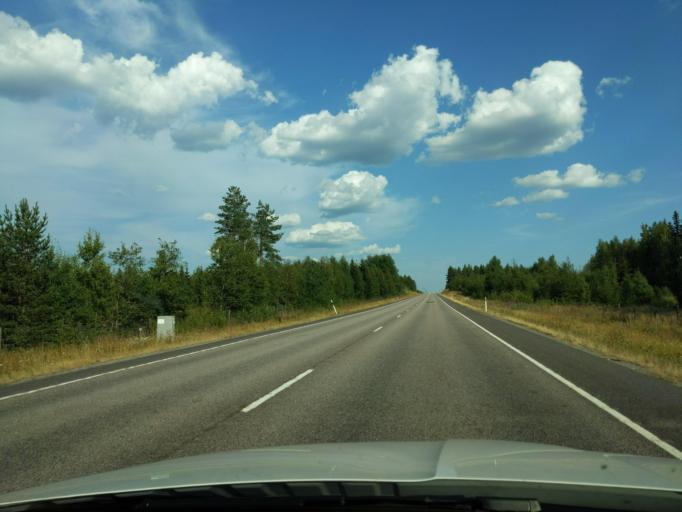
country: FI
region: Paijanne Tavastia
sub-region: Lahti
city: Hollola
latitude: 60.9921
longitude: 25.3757
